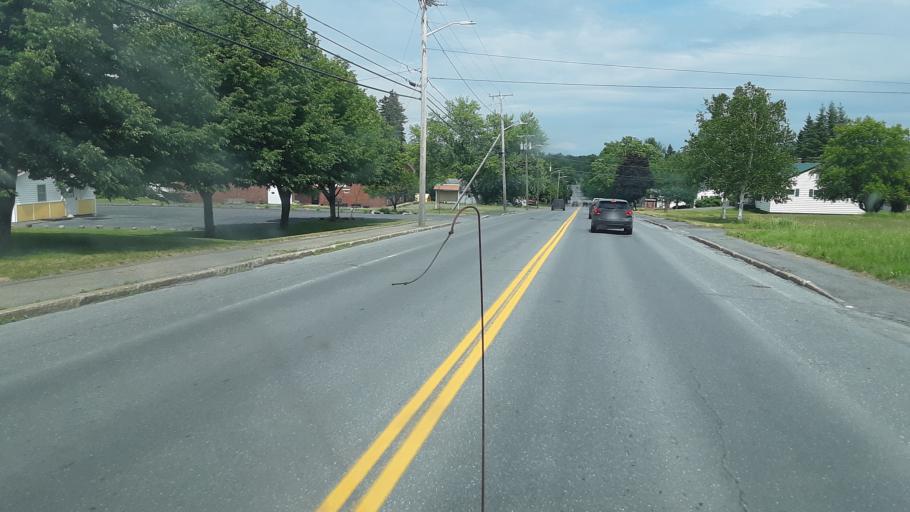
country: US
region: Maine
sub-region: Aroostook County
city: Fort Fairfield
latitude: 46.7679
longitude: -67.8445
